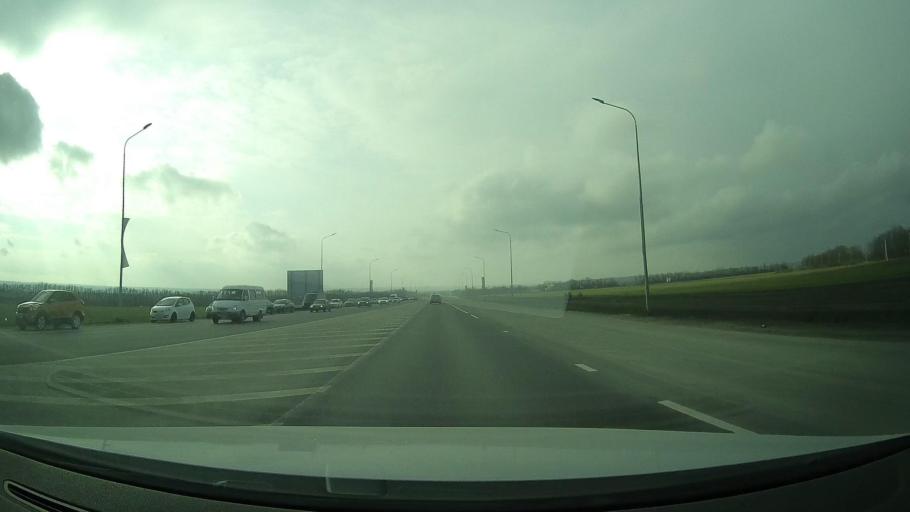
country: RU
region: Rostov
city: Grushevskaya
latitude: 47.4787
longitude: 39.9200
